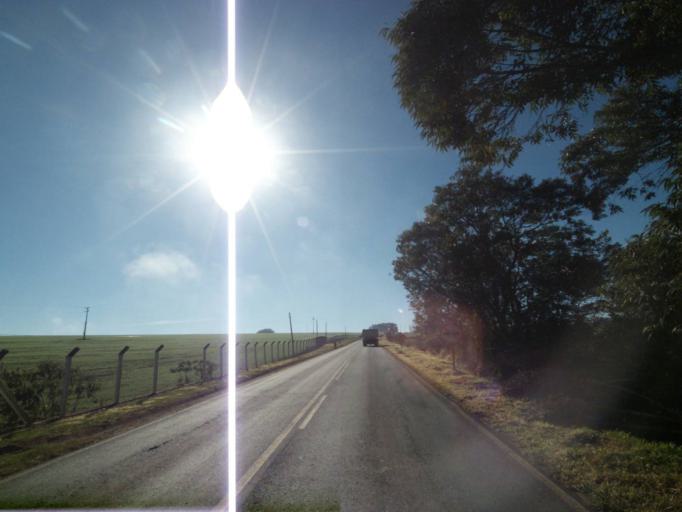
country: BR
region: Parana
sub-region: Tibagi
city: Tibagi
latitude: -24.5268
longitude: -50.3837
